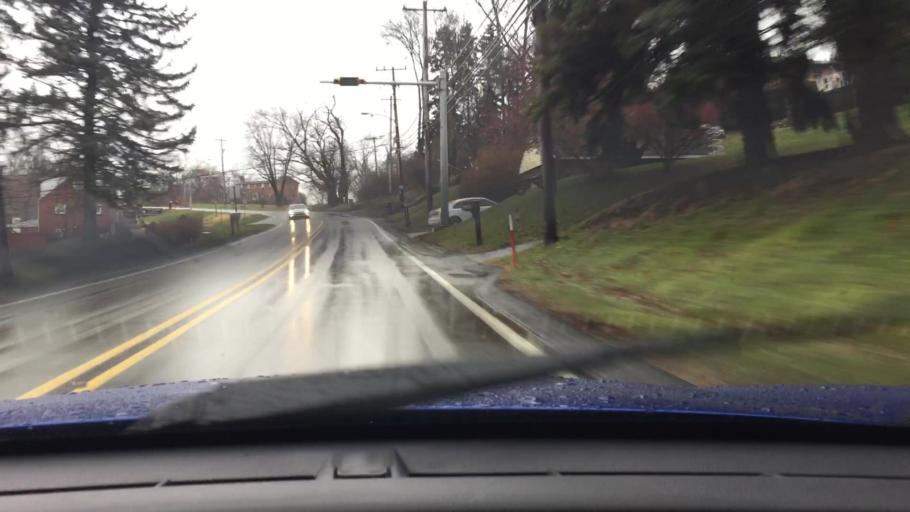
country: US
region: Pennsylvania
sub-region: Allegheny County
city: Wilson
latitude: 40.3146
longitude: -79.9170
